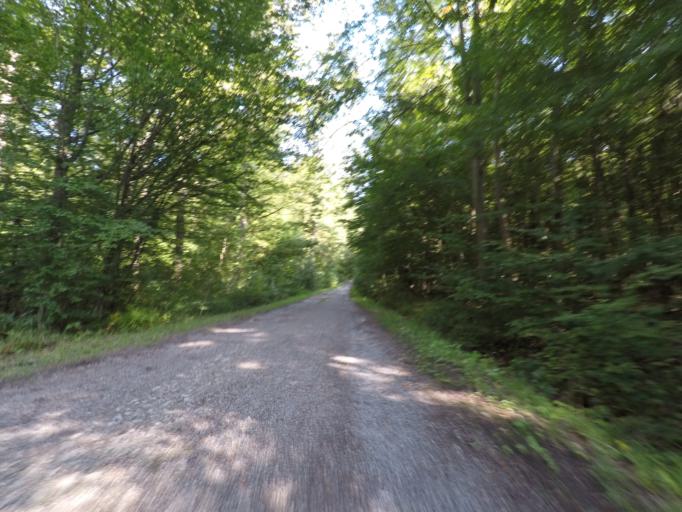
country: DE
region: Baden-Wuerttemberg
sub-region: Regierungsbezirk Stuttgart
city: Ehningen
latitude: 48.6700
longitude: 8.9727
